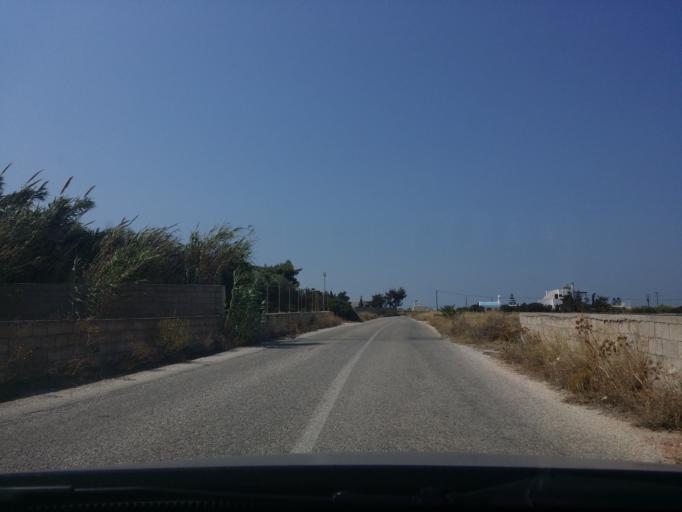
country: GR
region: South Aegean
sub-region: Nomos Kykladon
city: Antiparos
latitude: 37.0384
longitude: 25.1117
